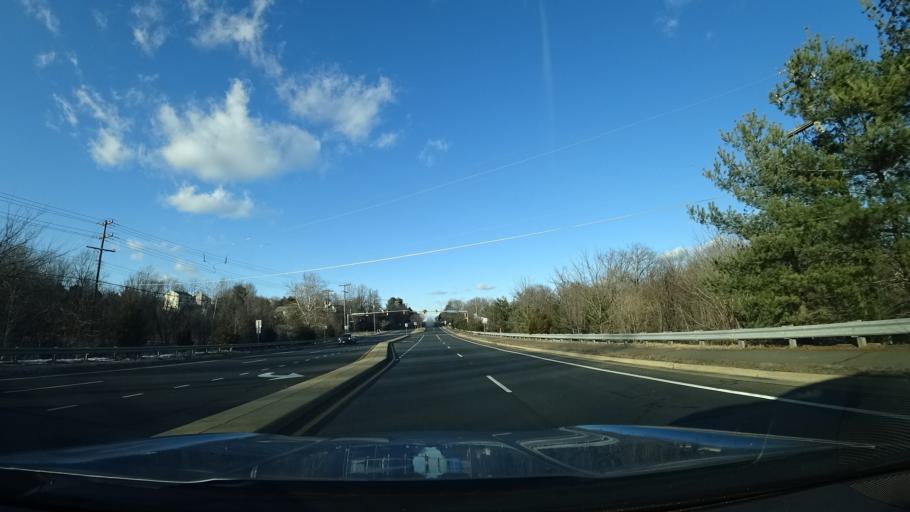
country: US
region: Virginia
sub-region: Fairfax County
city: Herndon
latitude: 38.9931
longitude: -77.3767
